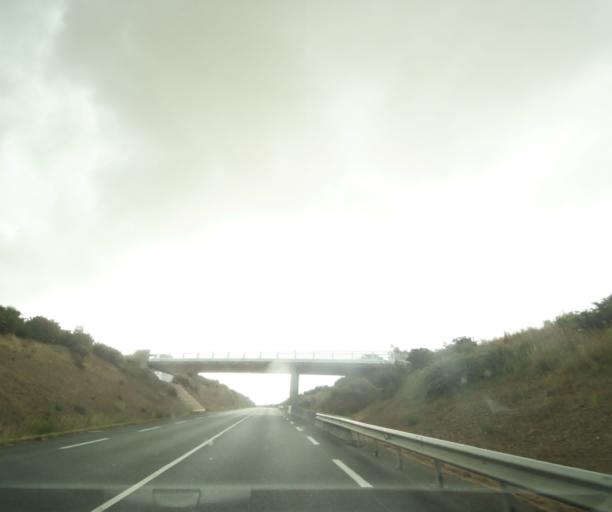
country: FR
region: Pays de la Loire
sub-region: Departement de la Vendee
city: Saint-Hilaire-de-Talmont
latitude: 46.4582
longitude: -1.6200
